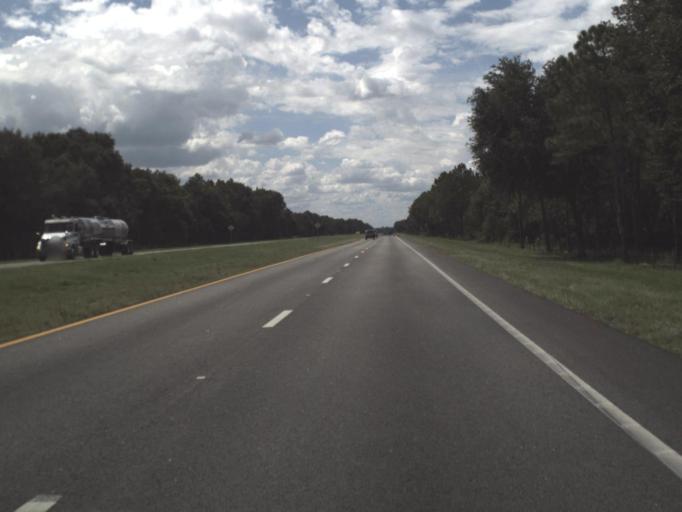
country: US
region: Florida
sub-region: Polk County
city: Alturas
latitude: 27.9053
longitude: -81.6664
